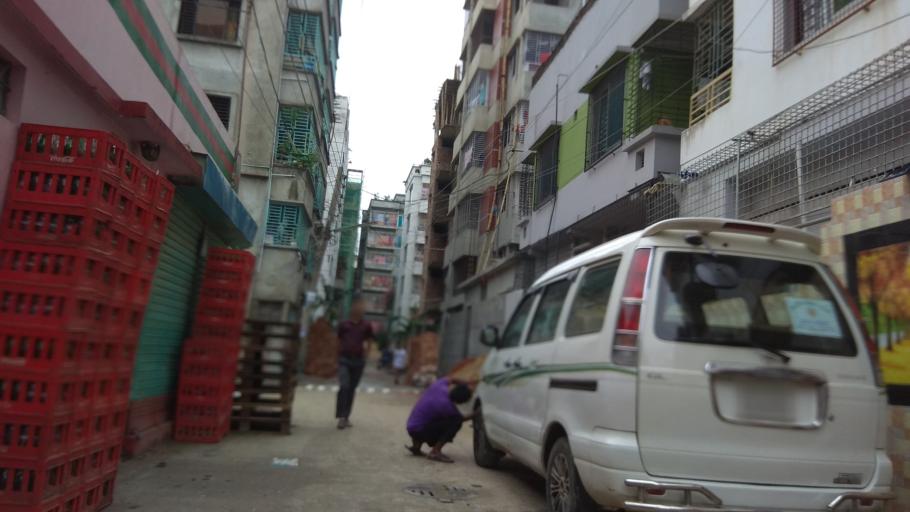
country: BD
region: Dhaka
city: Azimpur
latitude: 23.8008
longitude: 90.3604
